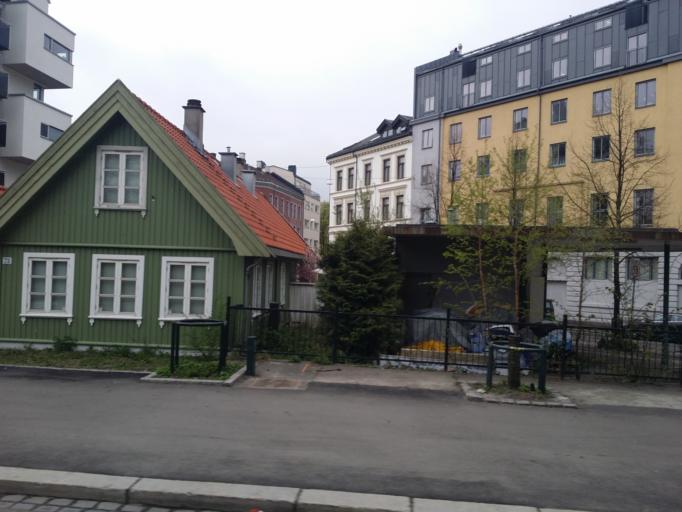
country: NO
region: Oslo
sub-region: Oslo
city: Oslo
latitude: 59.9076
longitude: 10.7816
